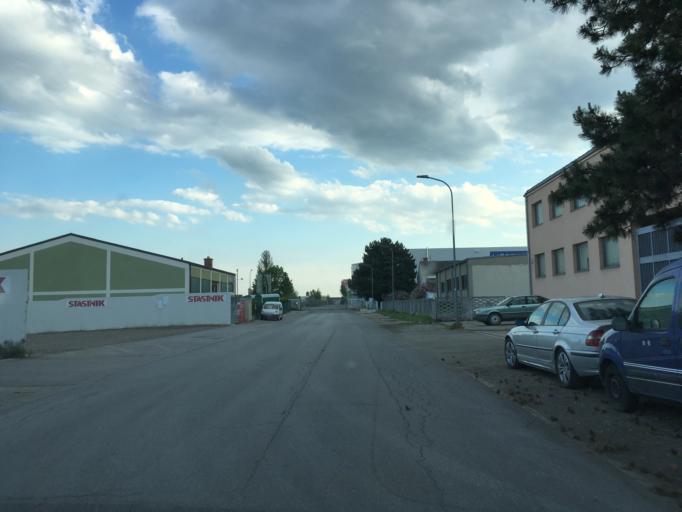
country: AT
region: Lower Austria
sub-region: Politischer Bezirk Wien-Umgebung
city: Gerasdorf bei Wien
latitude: 48.2829
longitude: 16.4814
